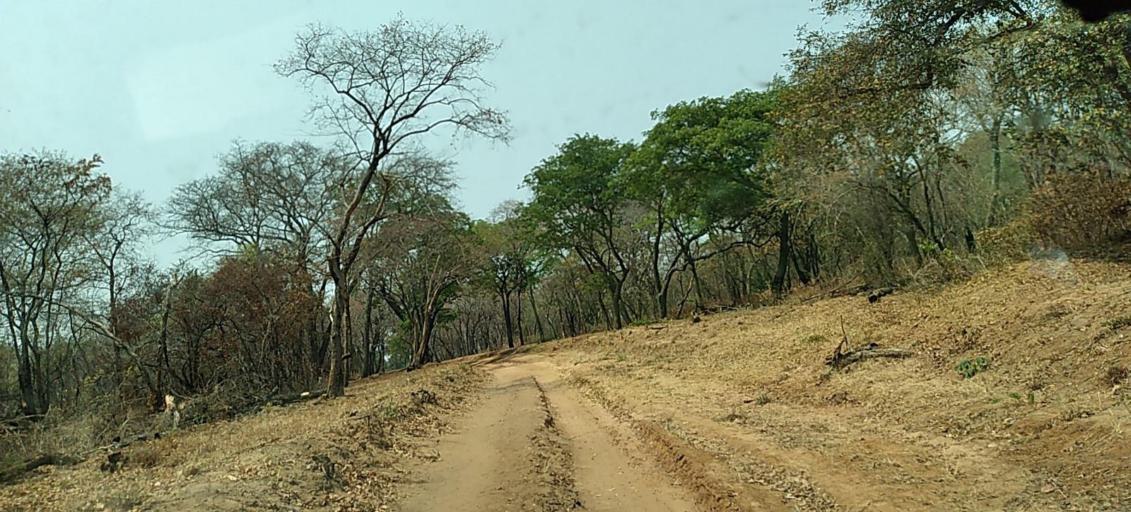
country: ZM
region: Western
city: Lukulu
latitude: -13.9853
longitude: 23.2287
